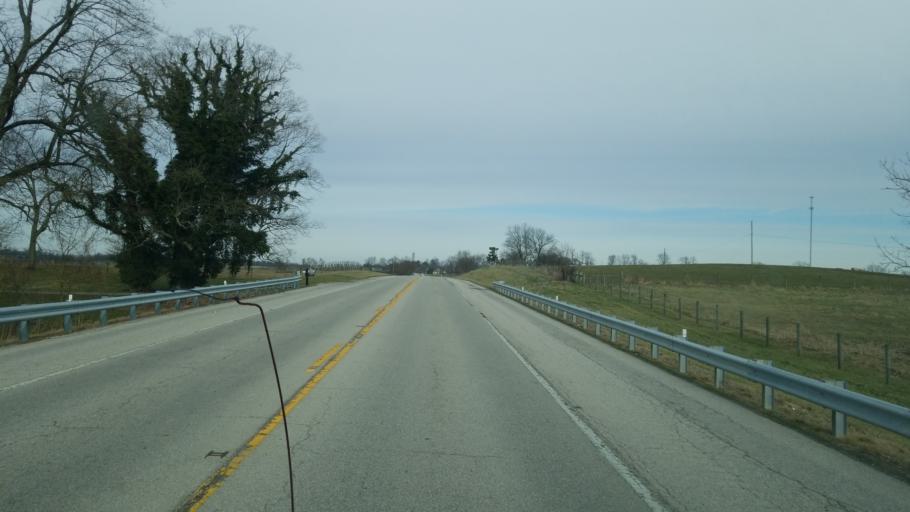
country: US
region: Kentucky
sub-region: Fleming County
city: Flemingsburg
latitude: 38.4920
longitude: -83.8562
